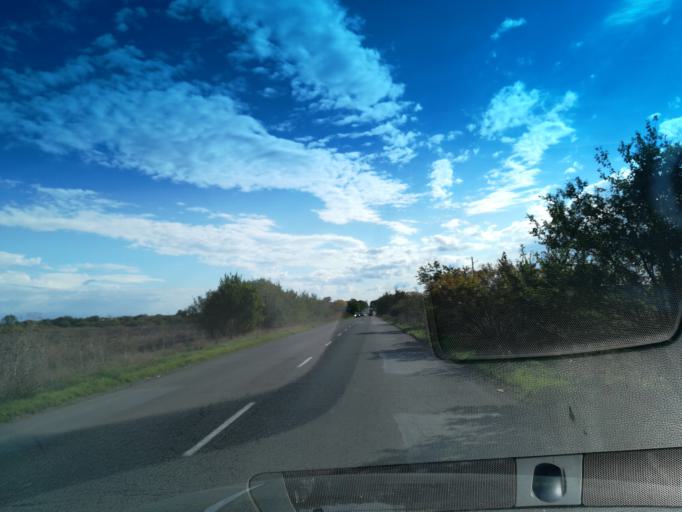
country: BG
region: Stara Zagora
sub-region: Obshtina Stara Zagora
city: Stara Zagora
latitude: 42.3643
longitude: 25.6549
